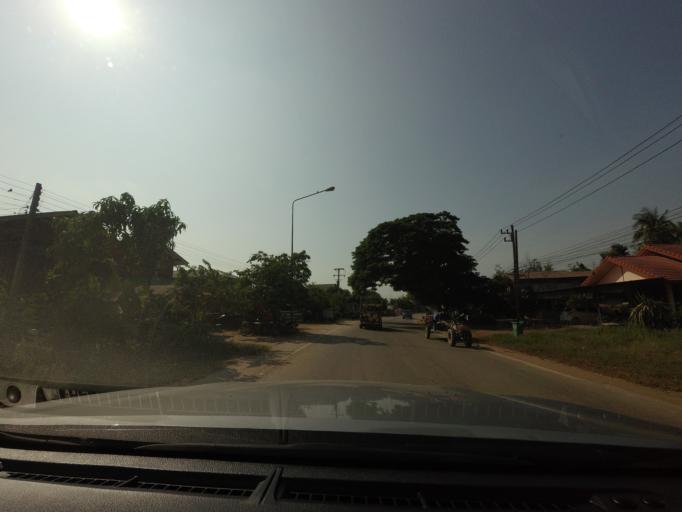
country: TH
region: Sukhothai
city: Kong Krailat
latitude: 16.8525
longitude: 99.9533
